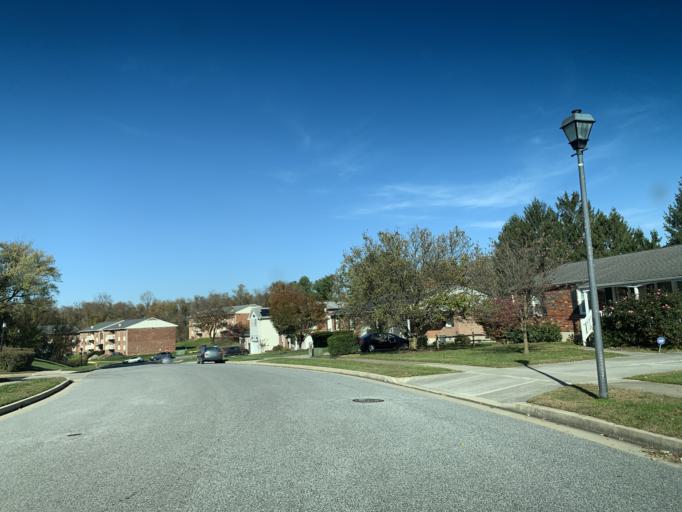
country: US
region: Maryland
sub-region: Baltimore County
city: Timonium
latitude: 39.4542
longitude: -76.6229
